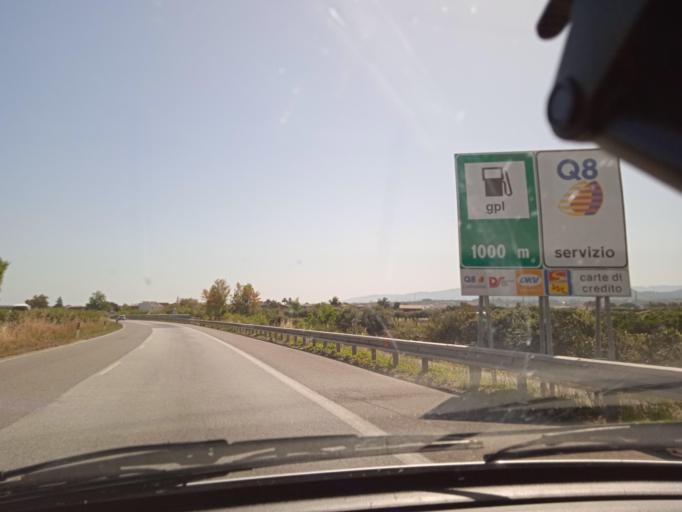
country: IT
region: Sicily
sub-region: Messina
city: Meri
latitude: 38.1763
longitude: 15.2420
